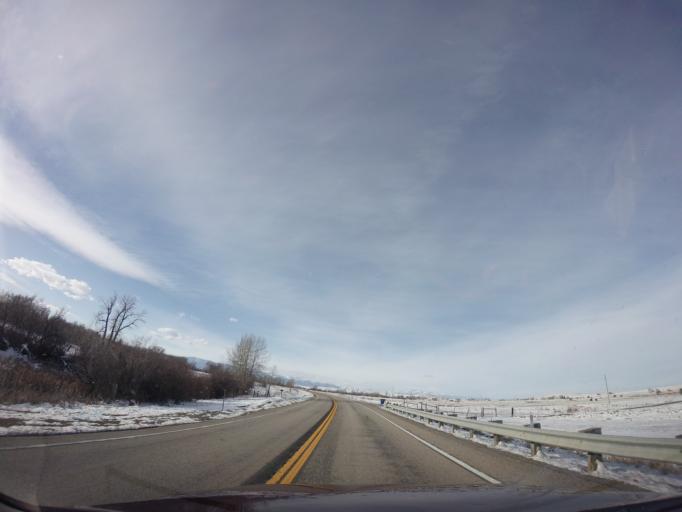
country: US
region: Montana
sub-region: Carbon County
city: Red Lodge
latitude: 45.3815
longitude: -109.1463
